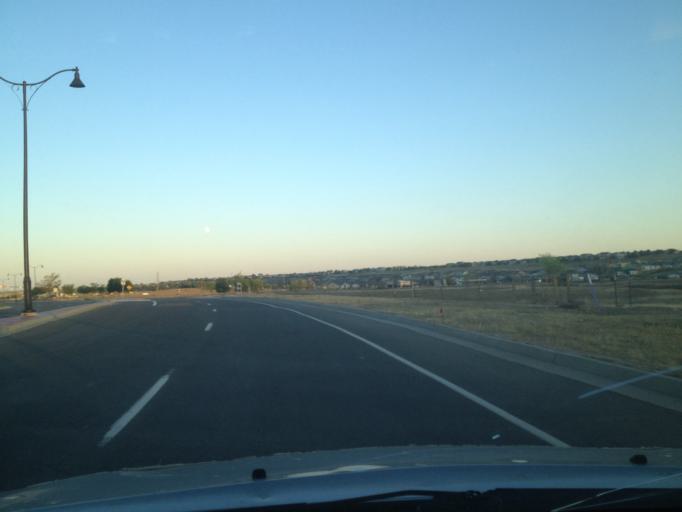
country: US
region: Colorado
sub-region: Boulder County
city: Superior
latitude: 39.8600
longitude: -105.1698
